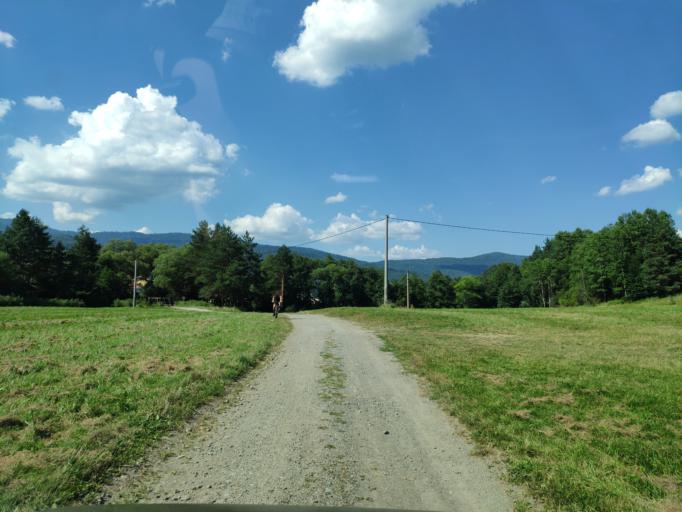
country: SK
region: Kosicky
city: Medzev
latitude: 48.7963
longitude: 20.8088
